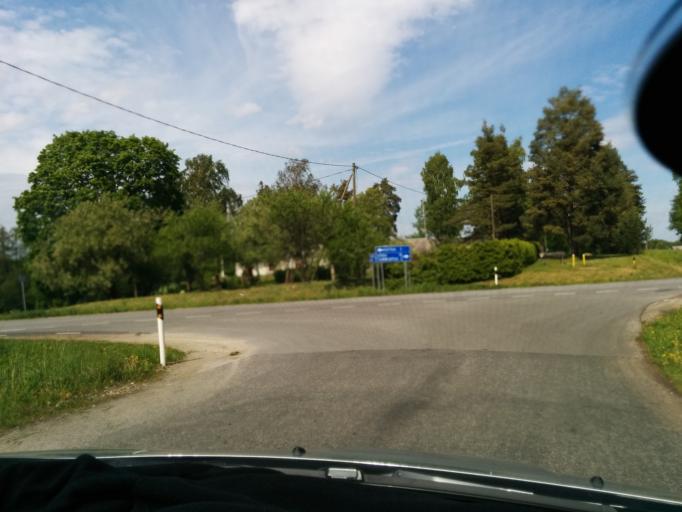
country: EE
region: Harju
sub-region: Loksa linn
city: Loksa
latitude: 59.5516
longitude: 25.7867
